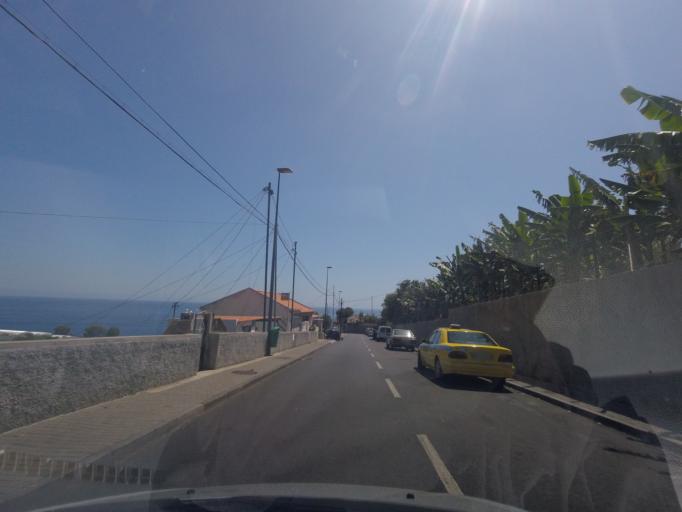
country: PT
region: Madeira
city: Camara de Lobos
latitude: 32.6486
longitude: -16.9612
